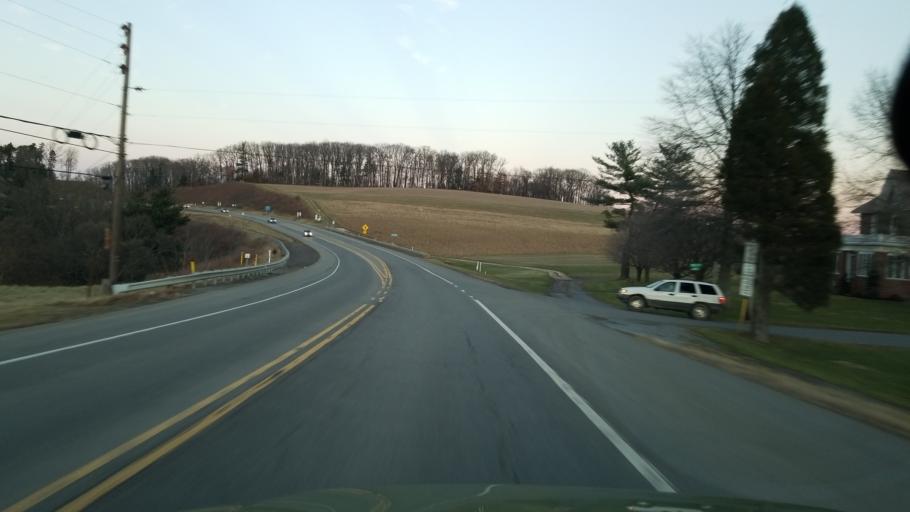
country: US
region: Pennsylvania
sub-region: Jefferson County
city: Punxsutawney
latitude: 40.9158
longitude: -78.9894
